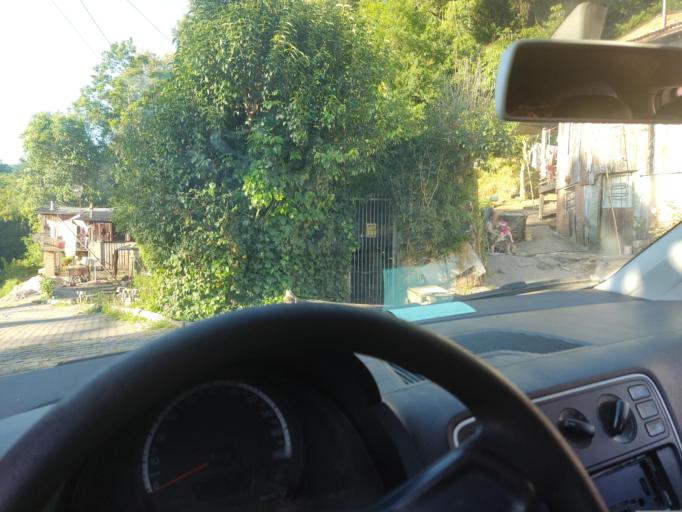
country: BR
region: Rio Grande do Sul
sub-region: Flores Da Cunha
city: Flores da Cunha
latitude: -28.8547
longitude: -51.2743
